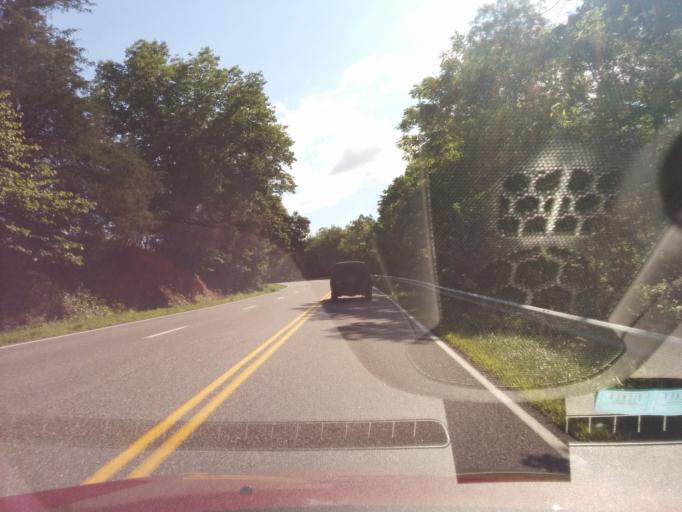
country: US
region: Virginia
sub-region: City of Lexington
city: Lexington
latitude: 37.7583
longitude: -79.4494
